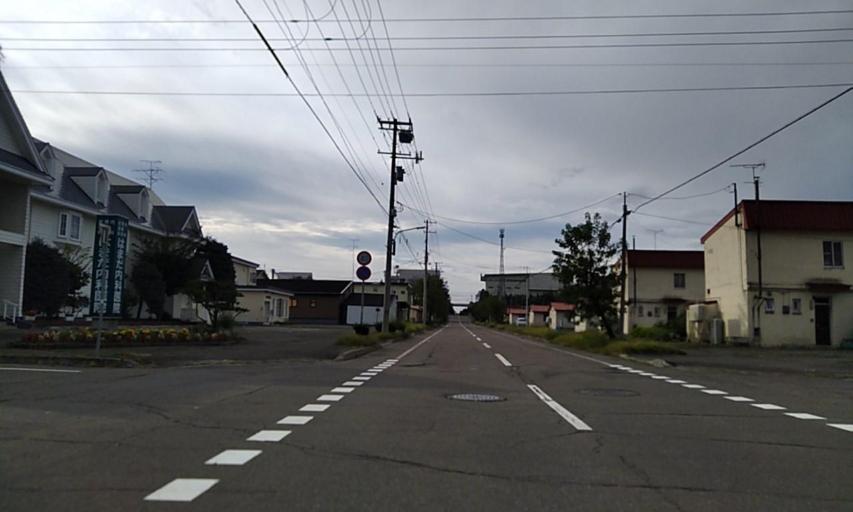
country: JP
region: Hokkaido
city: Obihiro
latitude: 42.9127
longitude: 143.0428
